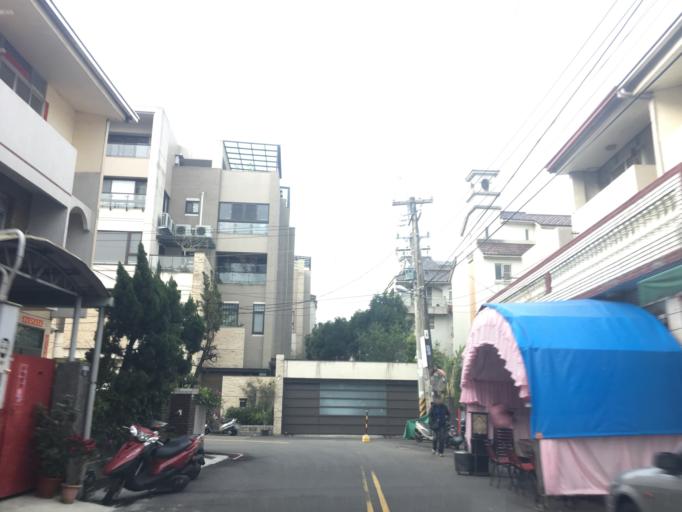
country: TW
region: Taiwan
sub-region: Taichung City
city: Taichung
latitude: 24.1890
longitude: 120.6995
